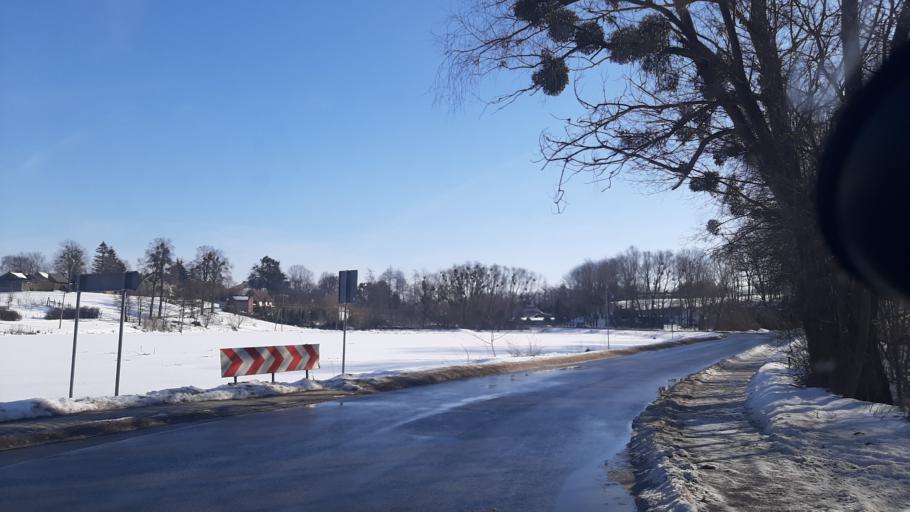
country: PL
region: Lublin Voivodeship
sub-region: Powiat pulawski
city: Wawolnica
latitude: 51.3570
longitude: 22.1228
